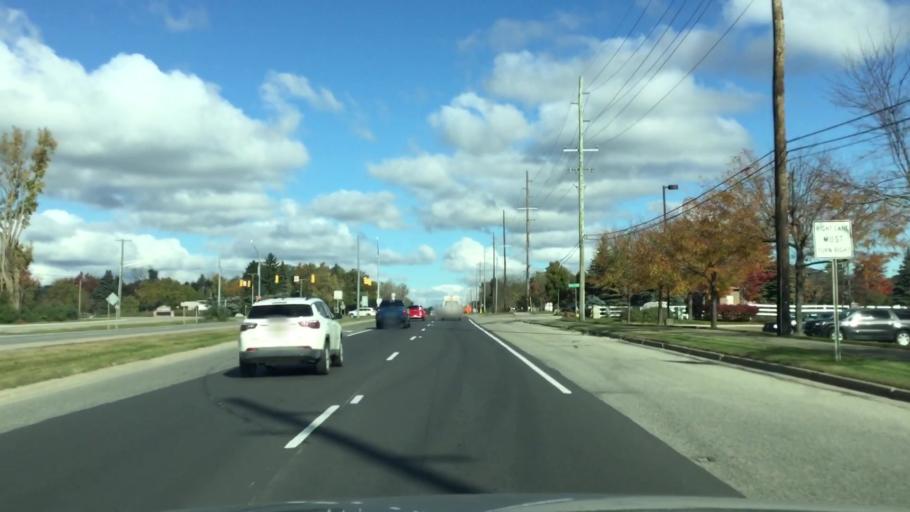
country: US
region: Michigan
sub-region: Oakland County
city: Lake Orion
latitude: 42.7907
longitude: -83.2458
